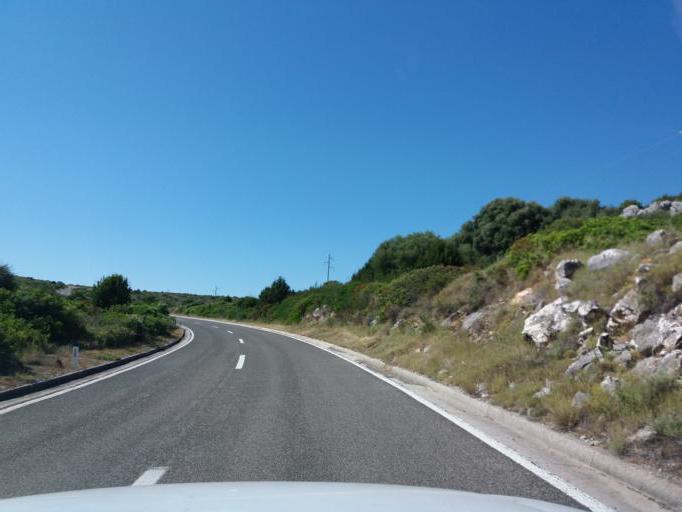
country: HR
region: Zadarska
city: Ugljan
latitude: 44.0233
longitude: 15.0354
